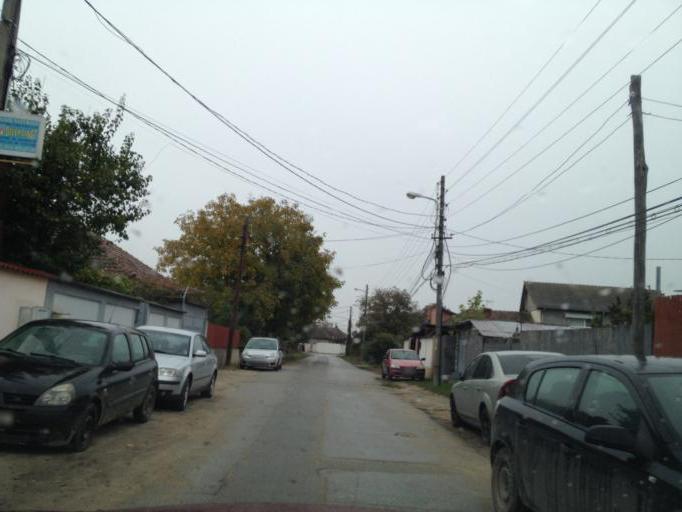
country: RO
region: Dolj
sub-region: Municipiul Craiova
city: Mofleni
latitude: 44.3103
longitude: 23.7768
